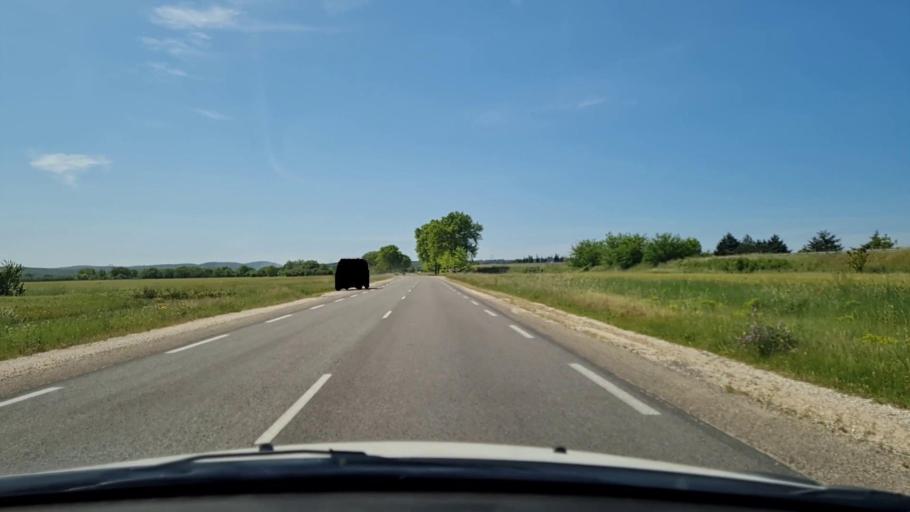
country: FR
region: Languedoc-Roussillon
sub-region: Departement du Gard
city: La Calmette
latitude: 43.9473
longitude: 4.2497
